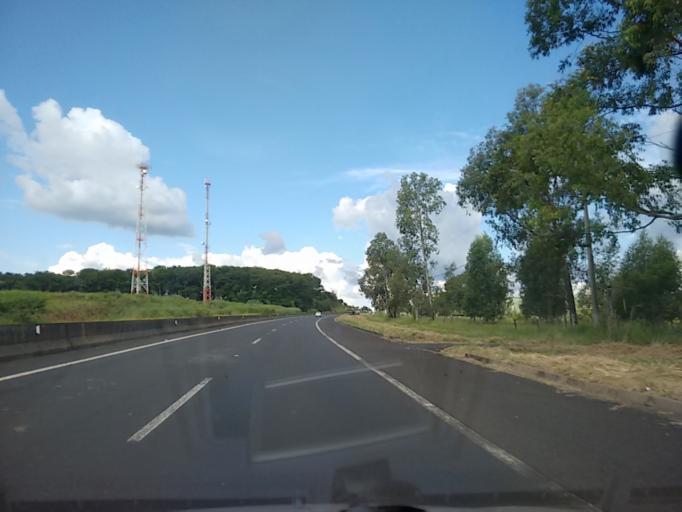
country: BR
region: Sao Paulo
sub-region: Marilia
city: Marilia
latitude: -22.2153
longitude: -49.8471
